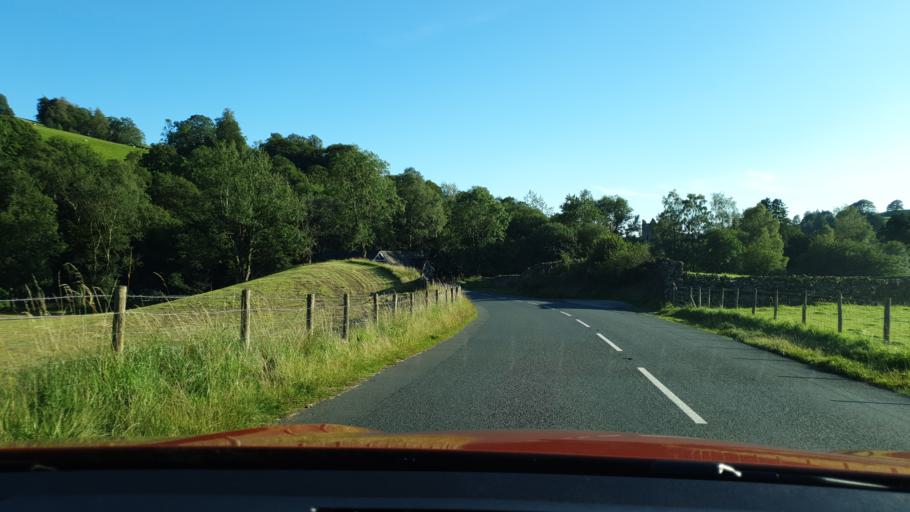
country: GB
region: England
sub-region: Cumbria
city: Windermere
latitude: 54.4185
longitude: -2.9048
